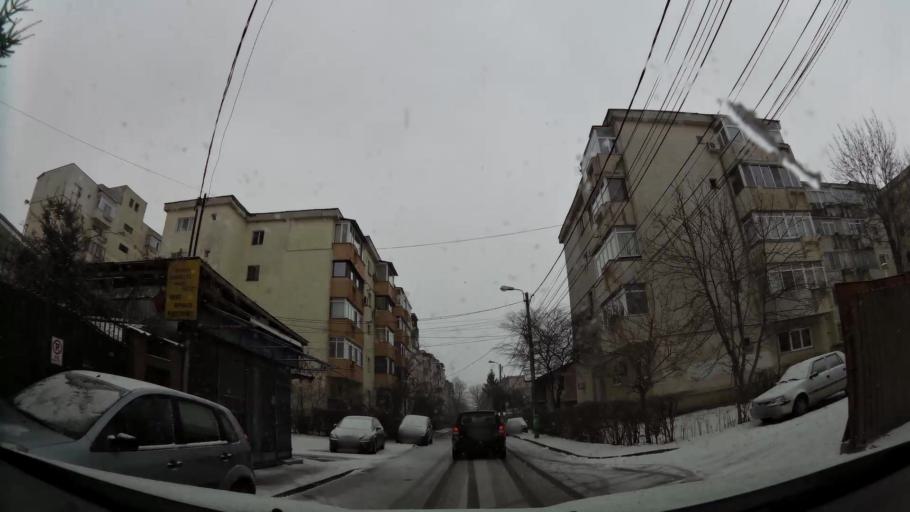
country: RO
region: Prahova
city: Ploiesti
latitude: 44.9316
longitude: 26.0059
